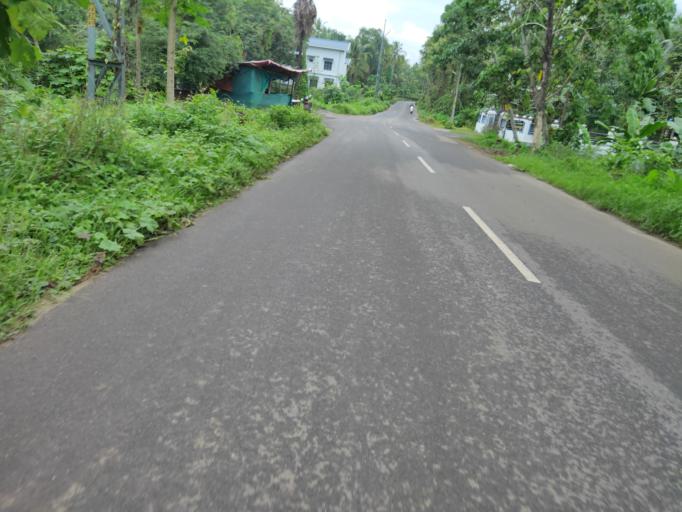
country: IN
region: Kerala
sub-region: Malappuram
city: Manjeri
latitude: 11.2276
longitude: 76.2741
